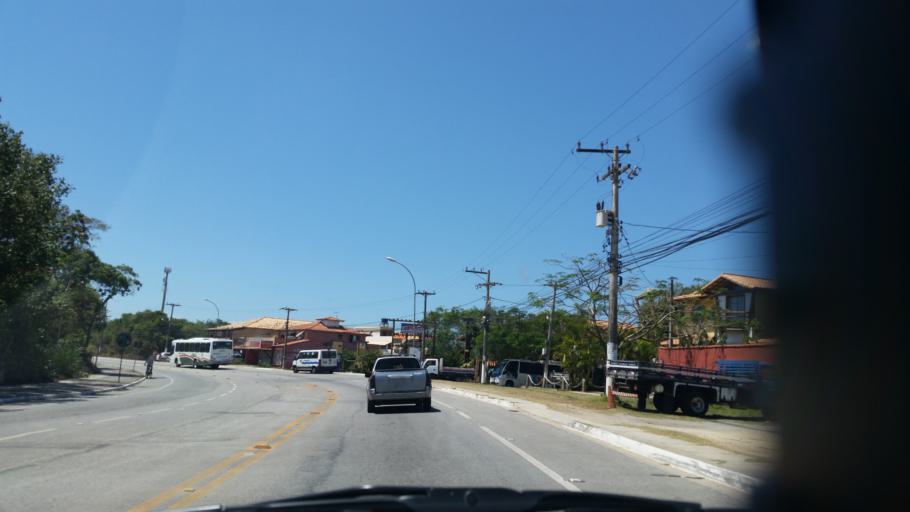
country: BR
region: Rio de Janeiro
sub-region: Armacao De Buzios
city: Armacao de Buzios
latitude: -22.7792
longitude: -41.9349
